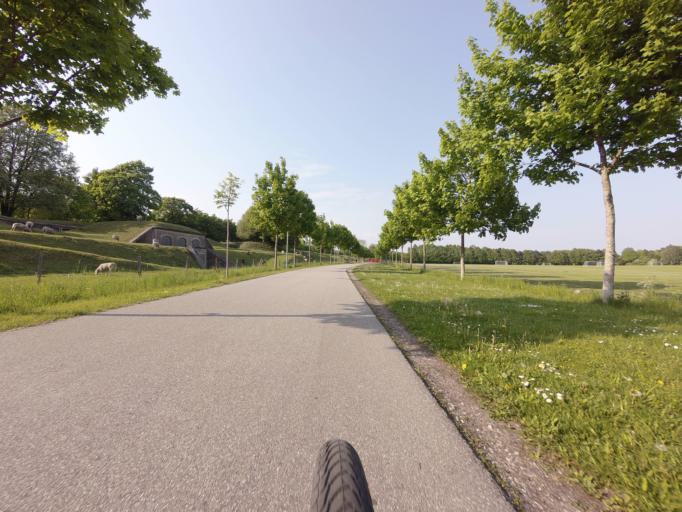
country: DK
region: Capital Region
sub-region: Rodovre Kommune
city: Rodovre
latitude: 55.6768
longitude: 12.4282
